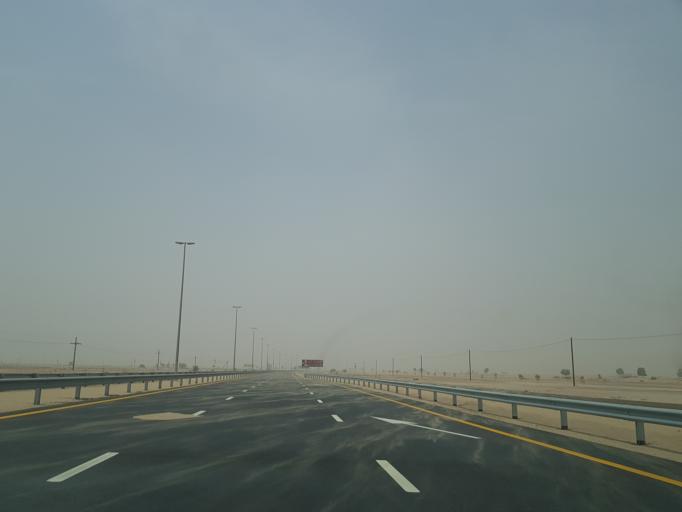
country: AE
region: Dubai
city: Dubai
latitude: 24.8983
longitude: 55.4302
